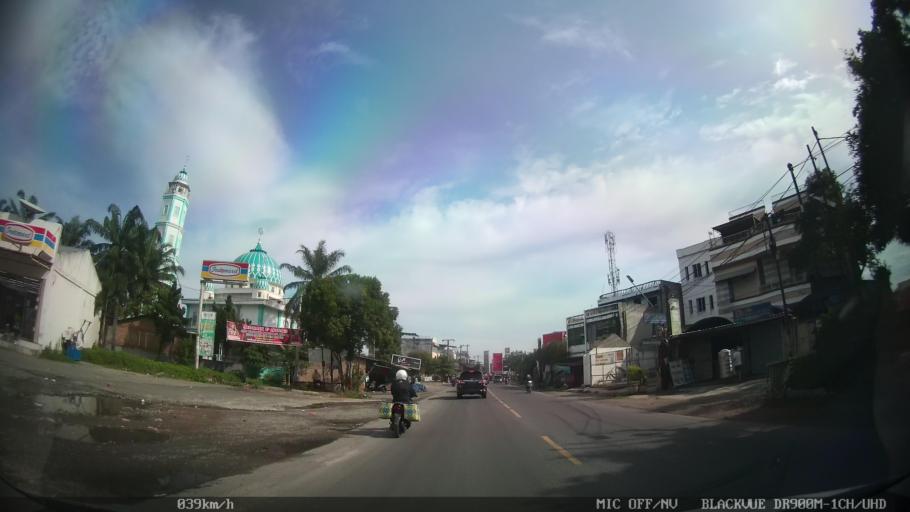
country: ID
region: North Sumatra
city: Medan
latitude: 3.6247
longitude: 98.6603
